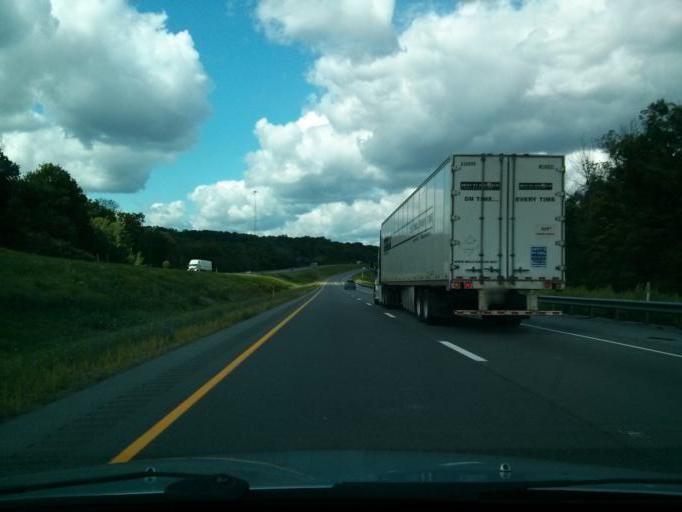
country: US
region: Pennsylvania
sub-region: Clearfield County
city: Treasure Lake
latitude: 41.1221
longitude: -78.6748
